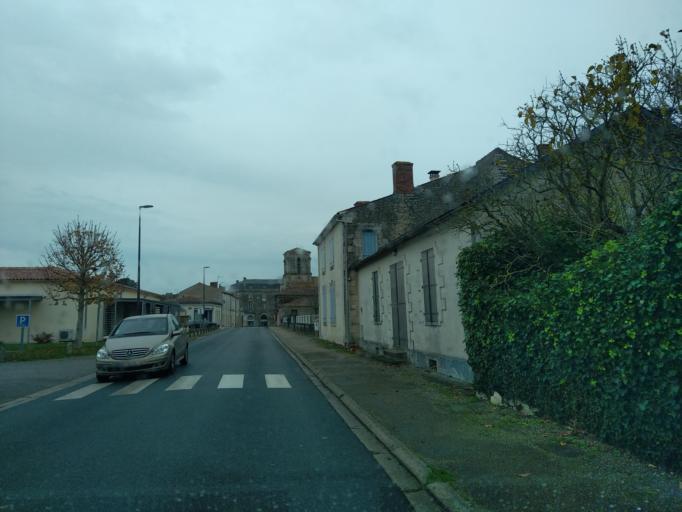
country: FR
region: Pays de la Loire
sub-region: Departement de la Vendee
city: Maillezais
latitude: 46.3700
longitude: -0.7399
